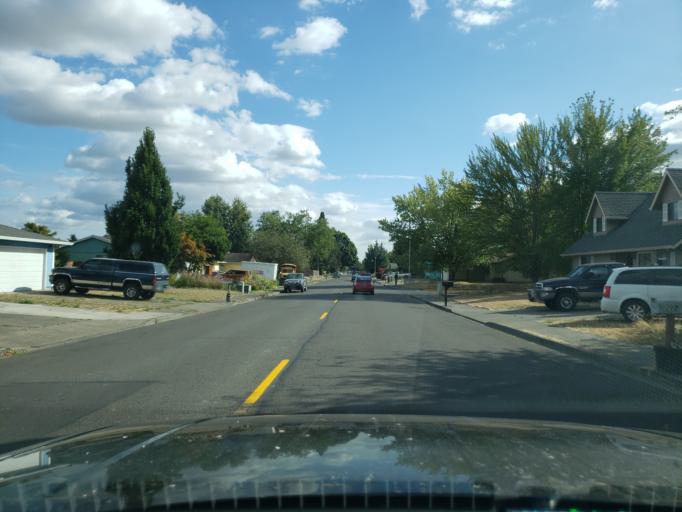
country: US
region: Oregon
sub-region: Yamhill County
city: McMinnville
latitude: 45.2083
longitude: -123.2196
